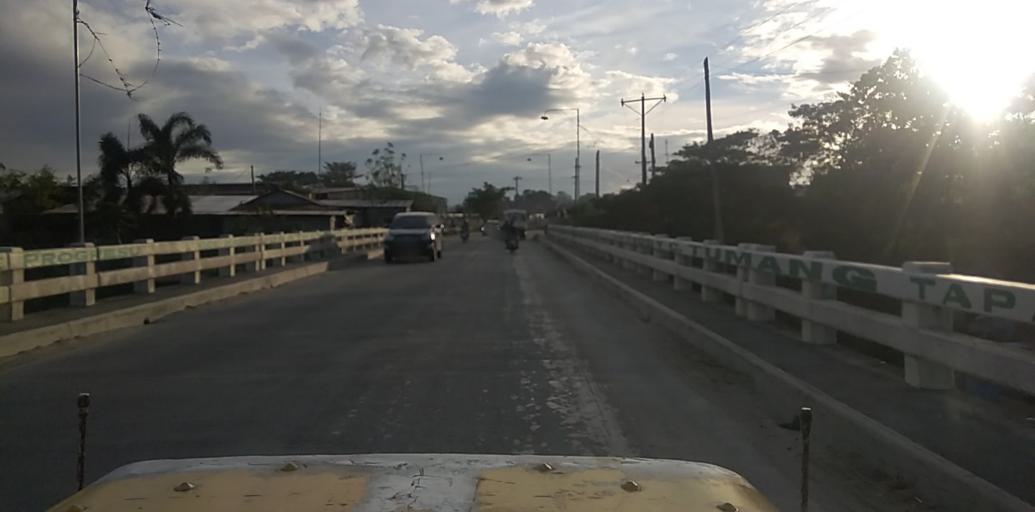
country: PH
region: Central Luzon
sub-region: Province of Pampanga
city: Malino
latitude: 15.1296
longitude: 120.6763
